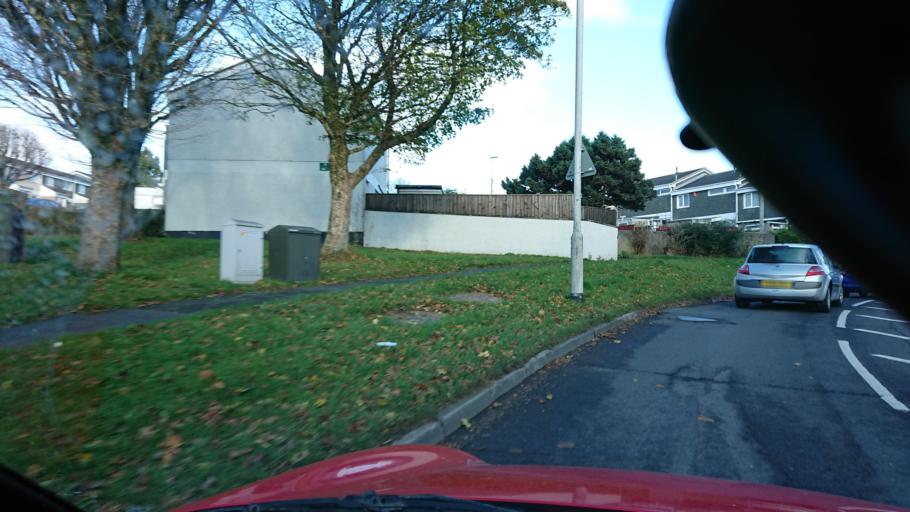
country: GB
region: England
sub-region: Plymouth
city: Plymouth
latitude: 50.4101
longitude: -4.1445
